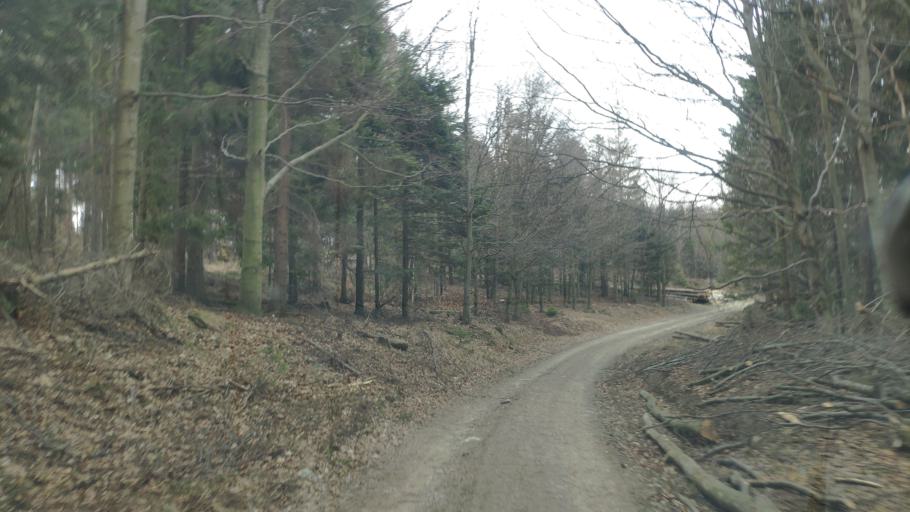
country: SK
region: Kosicky
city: Moldava nad Bodvou
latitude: 48.7526
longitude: 21.0418
